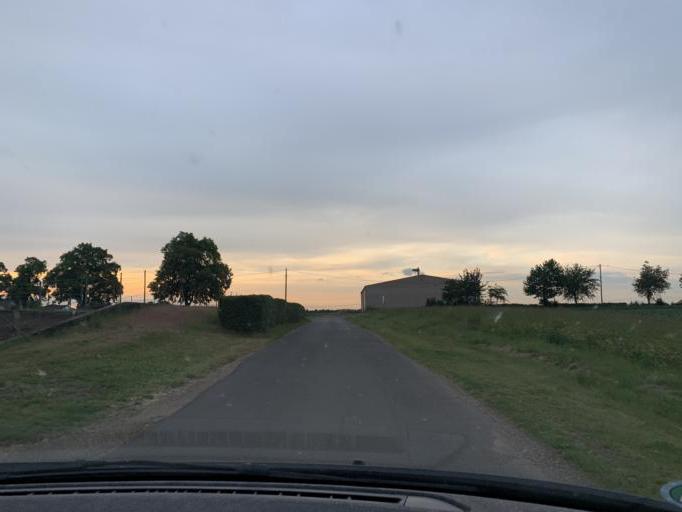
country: DE
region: North Rhine-Westphalia
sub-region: Regierungsbezirk Koln
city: Merzenich
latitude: 50.8396
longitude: 6.5855
